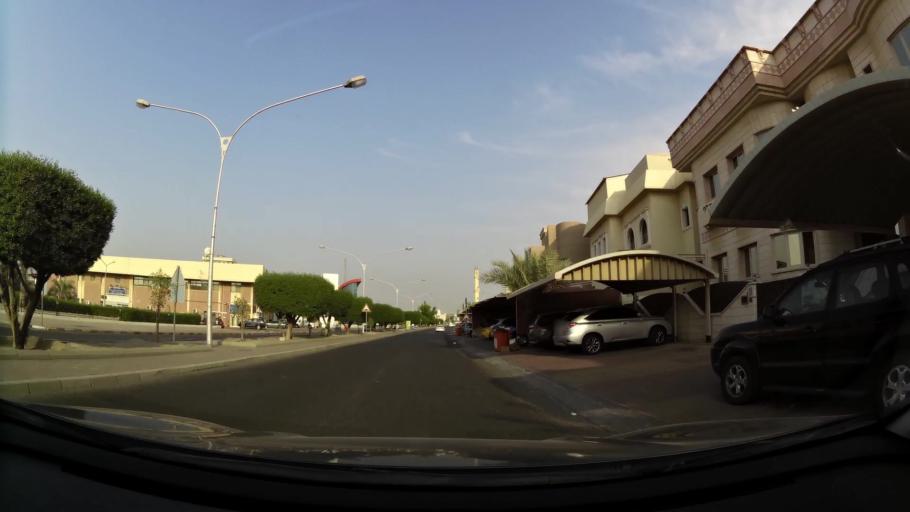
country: KW
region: Muhafazat Hawalli
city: Hawalli
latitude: 29.3124
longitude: 48.0017
